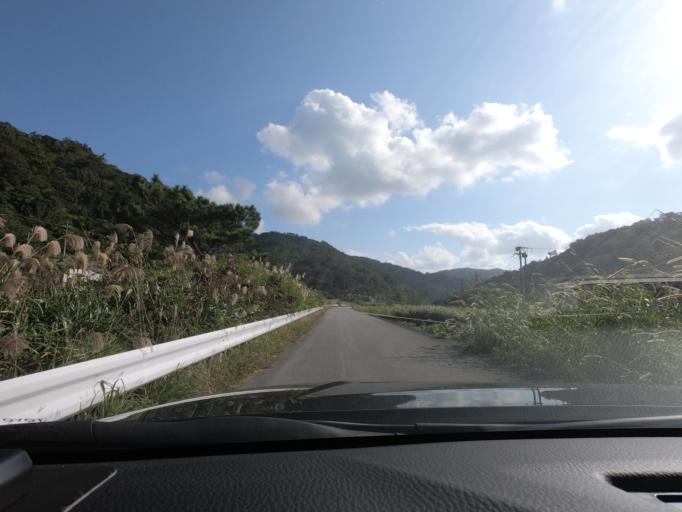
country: JP
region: Okinawa
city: Nago
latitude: 26.7664
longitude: 128.2066
